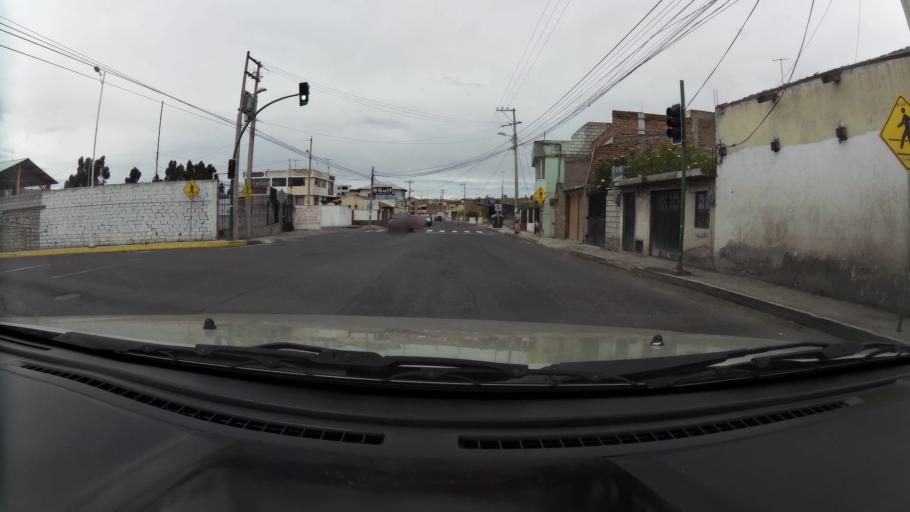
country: EC
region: Cotopaxi
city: Latacunga
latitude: -0.9487
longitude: -78.6112
